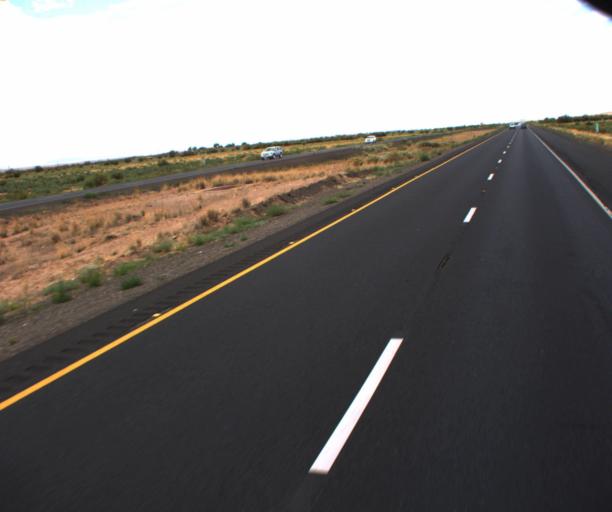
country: US
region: Arizona
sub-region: Navajo County
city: Winslow
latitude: 34.9850
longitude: -110.5537
